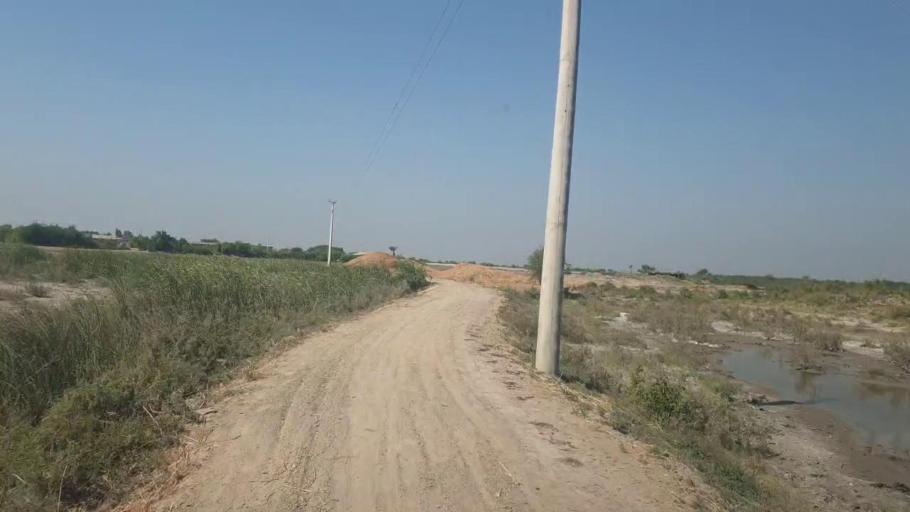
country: PK
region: Sindh
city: Badin
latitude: 24.6944
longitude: 68.8772
